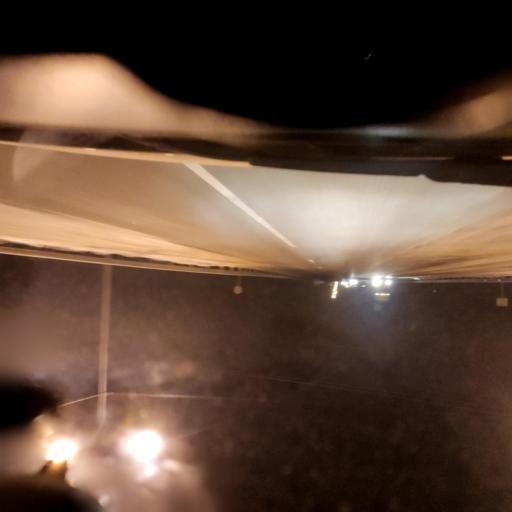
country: RU
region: Kursk
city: Fatezh
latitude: 52.0889
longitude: 35.8182
